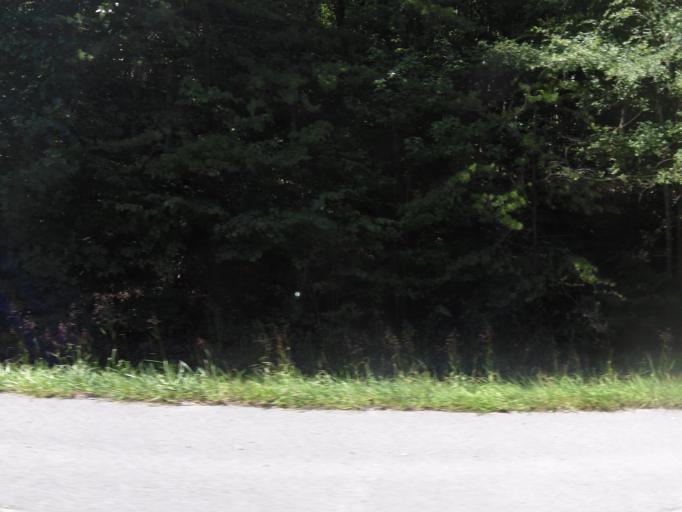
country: US
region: Kentucky
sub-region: Bell County
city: Pineville
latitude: 36.7716
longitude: -83.5915
